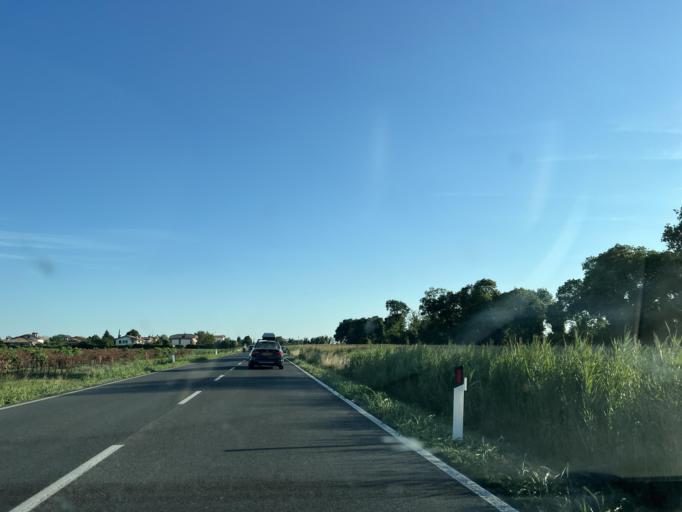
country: IT
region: Friuli Venezia Giulia
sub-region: Provincia di Gorizia
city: San Canzian d'Isonzo
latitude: 45.7610
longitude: 13.4695
